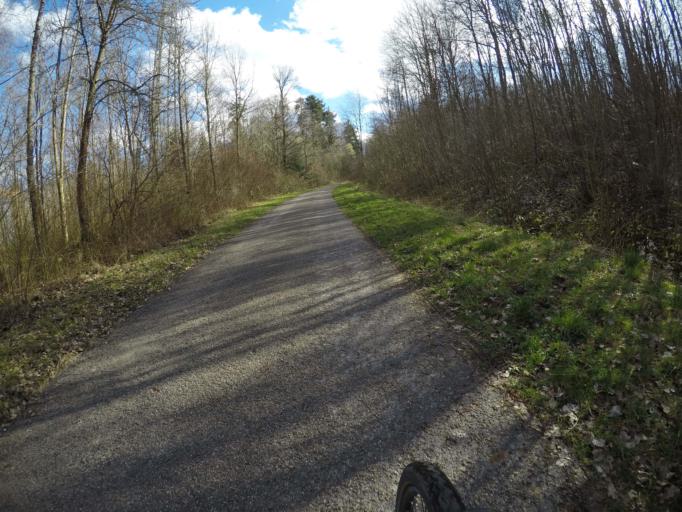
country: DE
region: Baden-Wuerttemberg
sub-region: Regierungsbezirk Stuttgart
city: Leinfelden-Echterdingen
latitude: 48.6857
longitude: 9.1421
